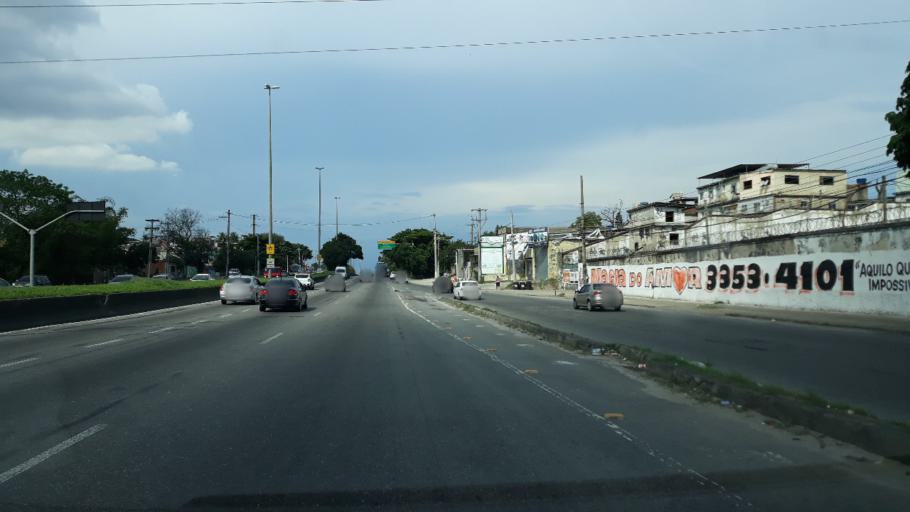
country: BR
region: Rio de Janeiro
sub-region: Sao Joao De Meriti
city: Sao Joao de Meriti
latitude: -22.8394
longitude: -43.3680
